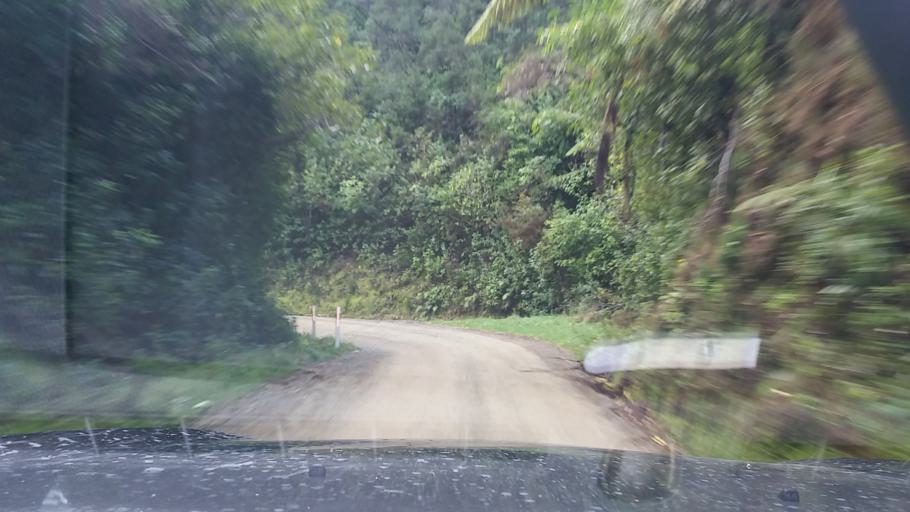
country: NZ
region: Marlborough
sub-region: Marlborough District
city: Picton
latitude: -41.1373
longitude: 174.1440
